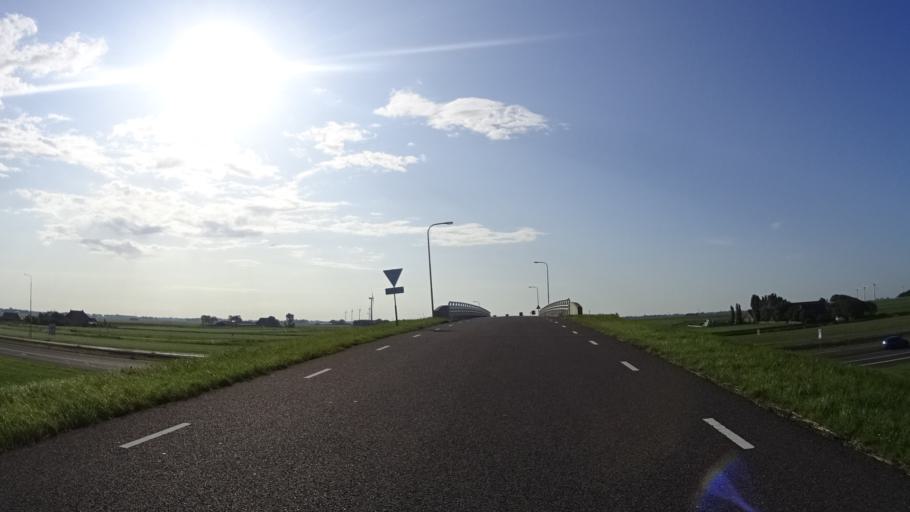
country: NL
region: Friesland
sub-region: Sudwest Fryslan
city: Makkum
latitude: 53.1069
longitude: 5.3895
